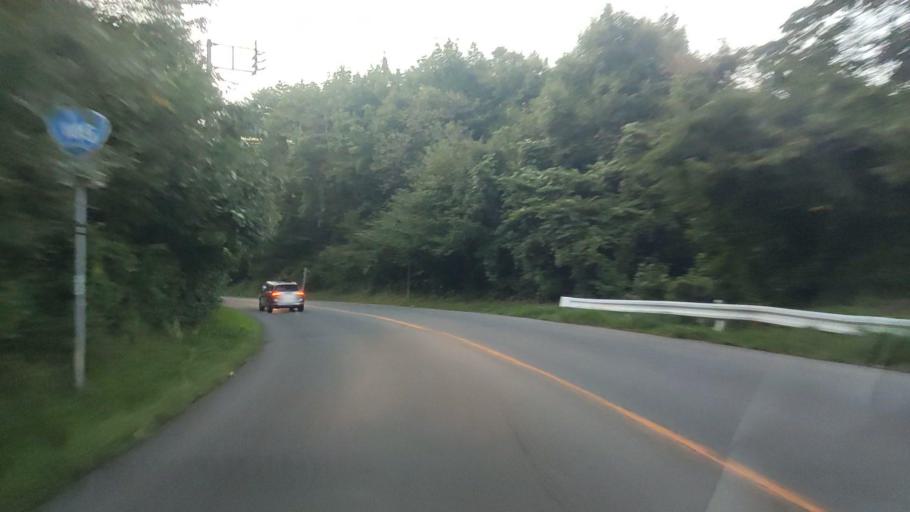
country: JP
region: Gunma
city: Nakanojomachi
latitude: 36.5322
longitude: 138.6105
